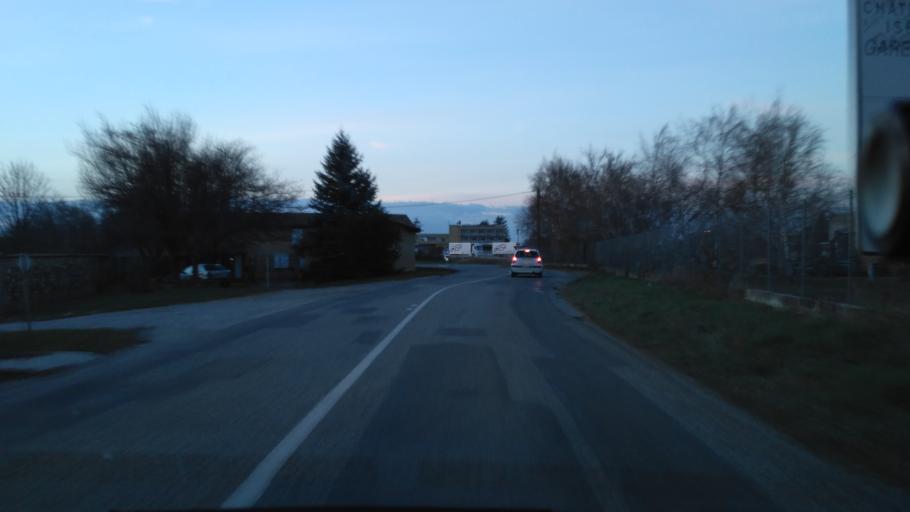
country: FR
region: Rhone-Alpes
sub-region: Departement de la Drome
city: Alixan
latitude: 44.9963
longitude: 5.0016
